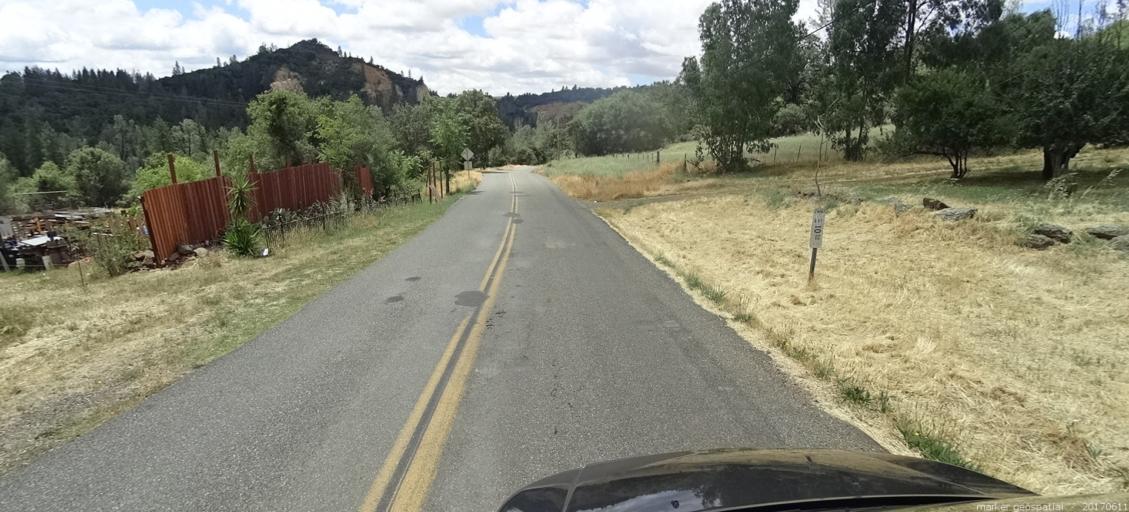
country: US
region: California
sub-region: Butte County
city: Oroville
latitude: 39.6456
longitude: -121.5390
